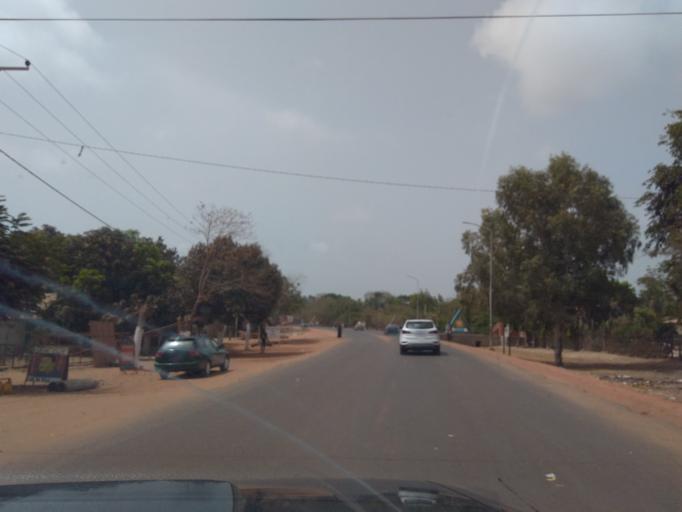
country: GM
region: Western
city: Sukuta
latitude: 13.4412
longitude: -16.7032
